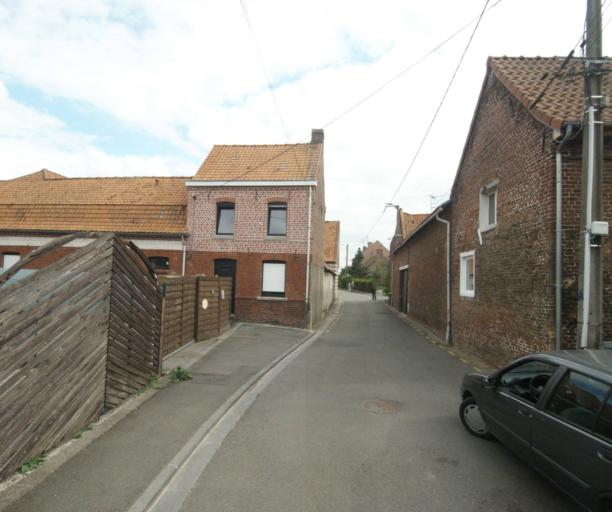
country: FR
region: Nord-Pas-de-Calais
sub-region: Departement du Nord
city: Anstaing
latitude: 50.6032
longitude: 3.1912
